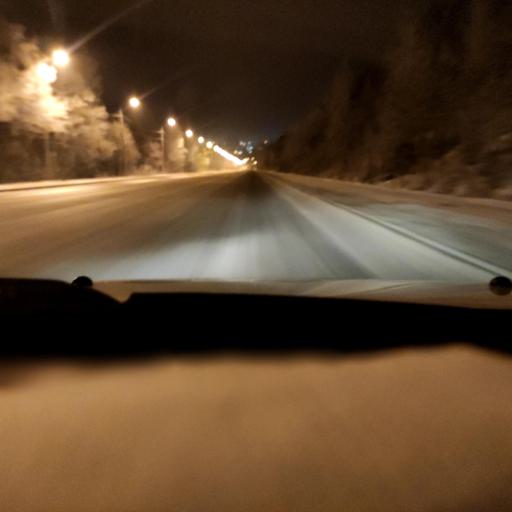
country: RU
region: Perm
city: Kondratovo
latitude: 57.9482
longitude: 56.1753
